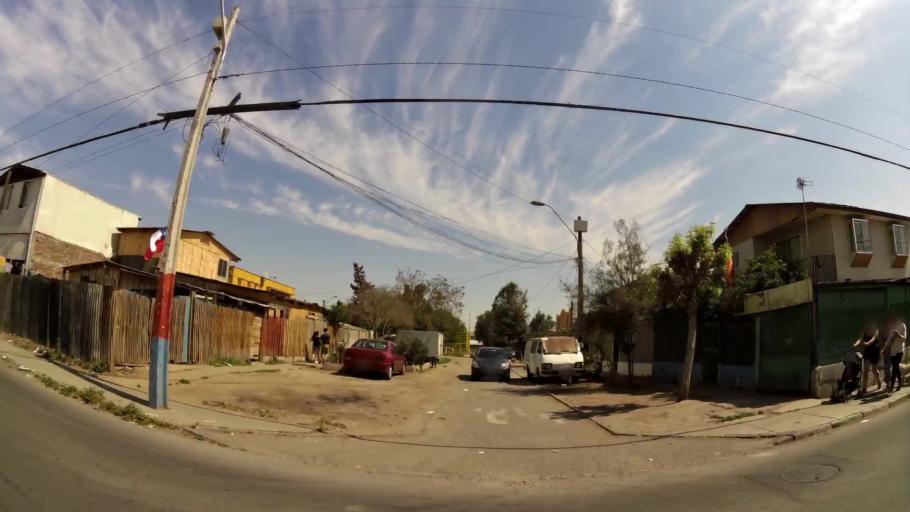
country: CL
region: Santiago Metropolitan
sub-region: Provincia de Santiago
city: La Pintana
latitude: -33.5540
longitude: -70.6369
